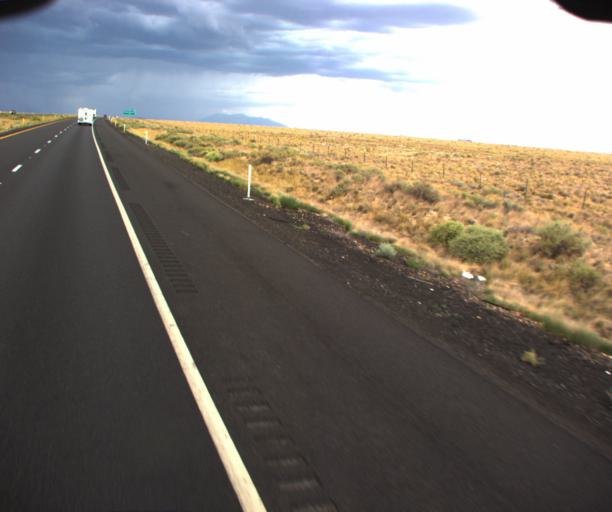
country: US
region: Arizona
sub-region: Coconino County
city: LeChee
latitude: 35.1217
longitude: -111.1600
